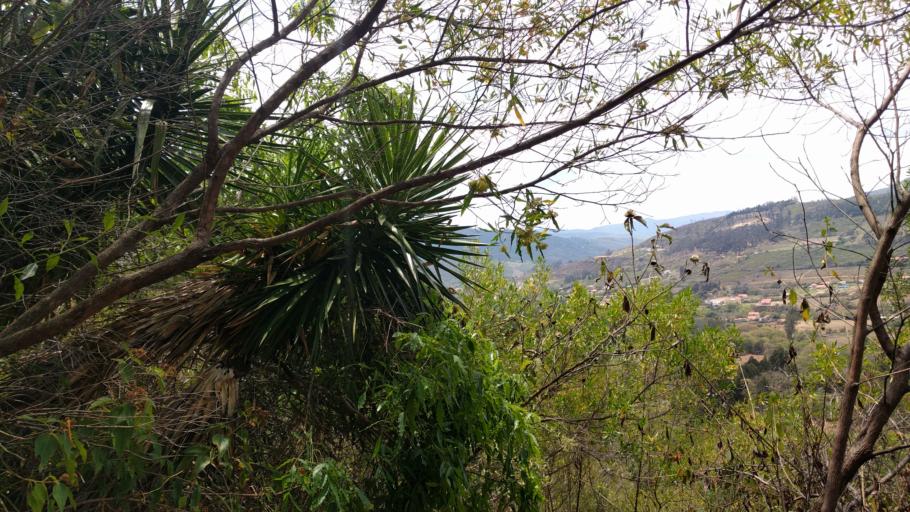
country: BO
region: Santa Cruz
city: Samaipata
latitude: -18.1883
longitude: -63.8821
